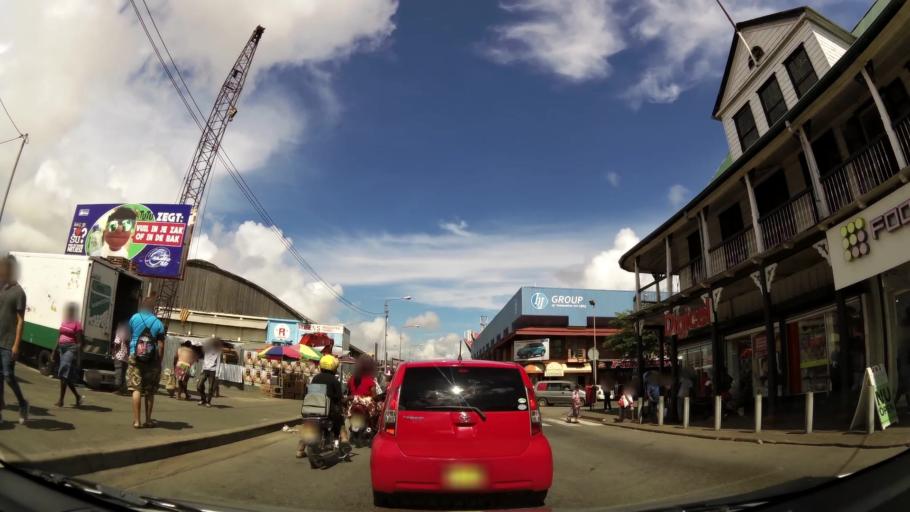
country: SR
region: Paramaribo
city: Paramaribo
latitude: 5.8239
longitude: -55.1581
